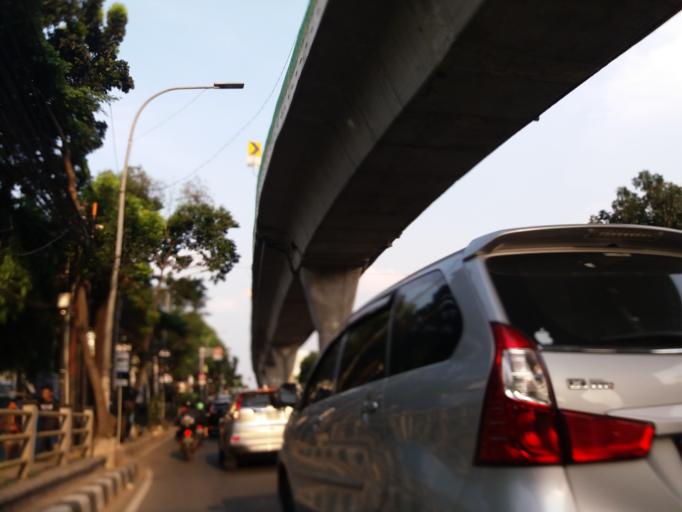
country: ID
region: Jakarta Raya
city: Jakarta
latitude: -6.2389
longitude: 106.8177
